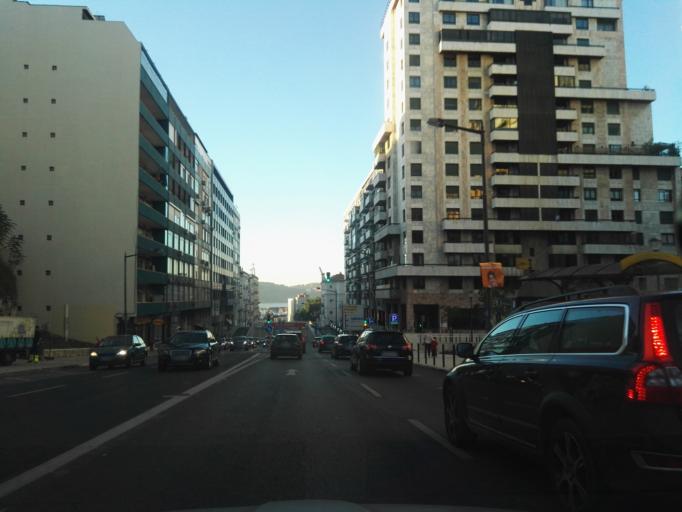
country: PT
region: Setubal
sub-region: Almada
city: Cacilhas
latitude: 38.7073
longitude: -9.1675
